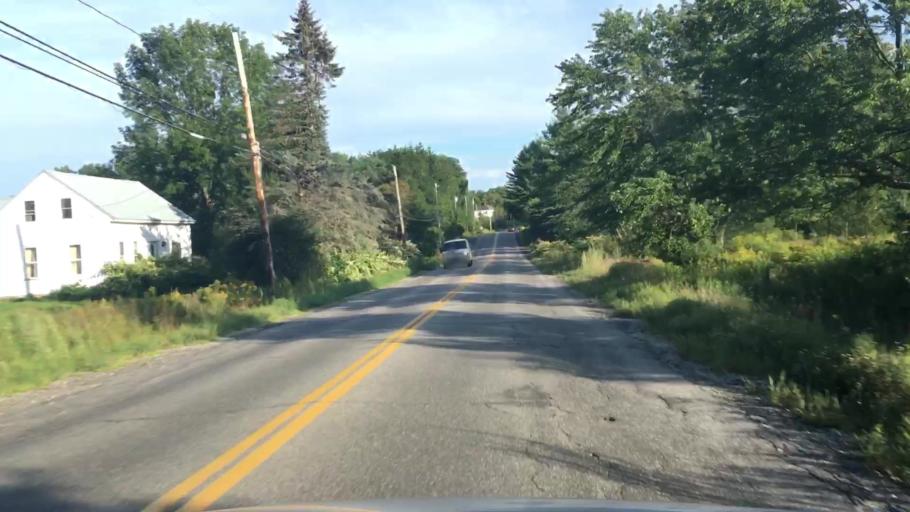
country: US
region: Maine
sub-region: Cumberland County
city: Westbrook
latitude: 43.7093
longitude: -70.3833
